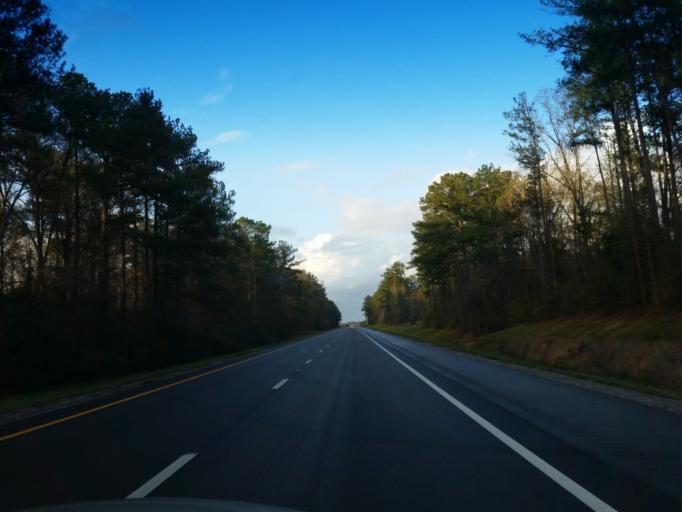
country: US
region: Mississippi
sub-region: Jones County
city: Sharon
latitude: 31.8531
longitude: -89.0477
